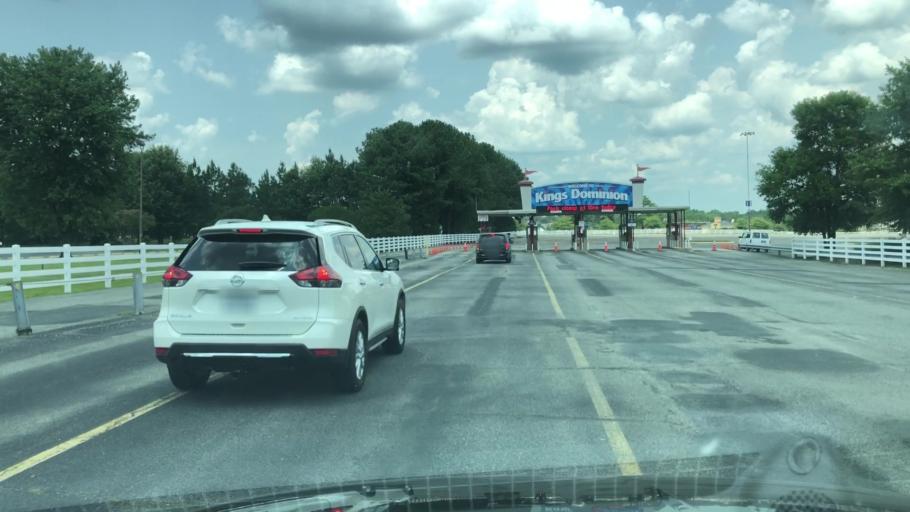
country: US
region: Virginia
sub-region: Hanover County
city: Ashland
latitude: 37.8436
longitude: -77.4484
